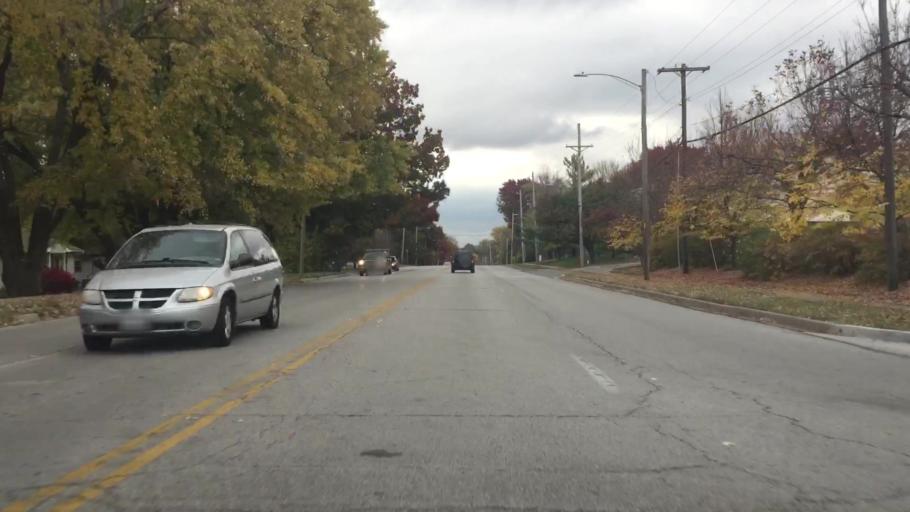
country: US
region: Missouri
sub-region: Jackson County
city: Raytown
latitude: 38.9946
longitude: -94.4705
